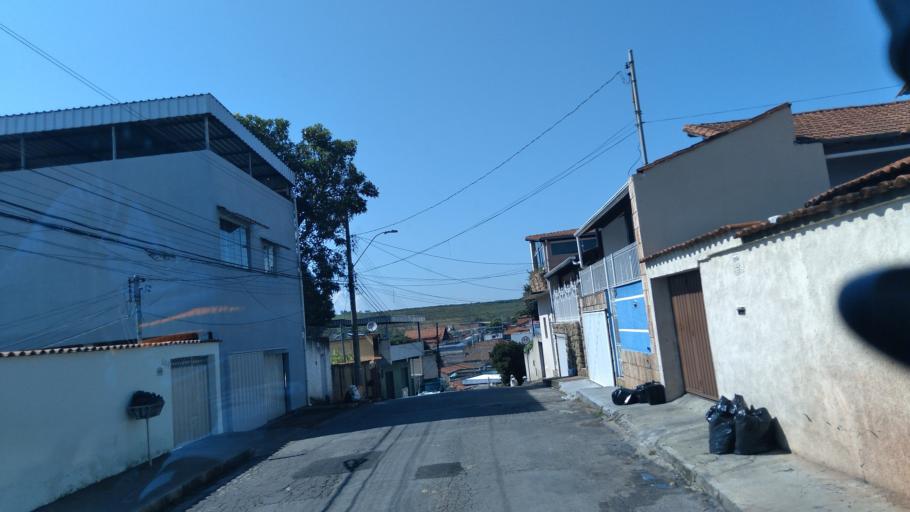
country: BR
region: Minas Gerais
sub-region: Contagem
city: Contagem
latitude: -19.9027
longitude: -44.0229
